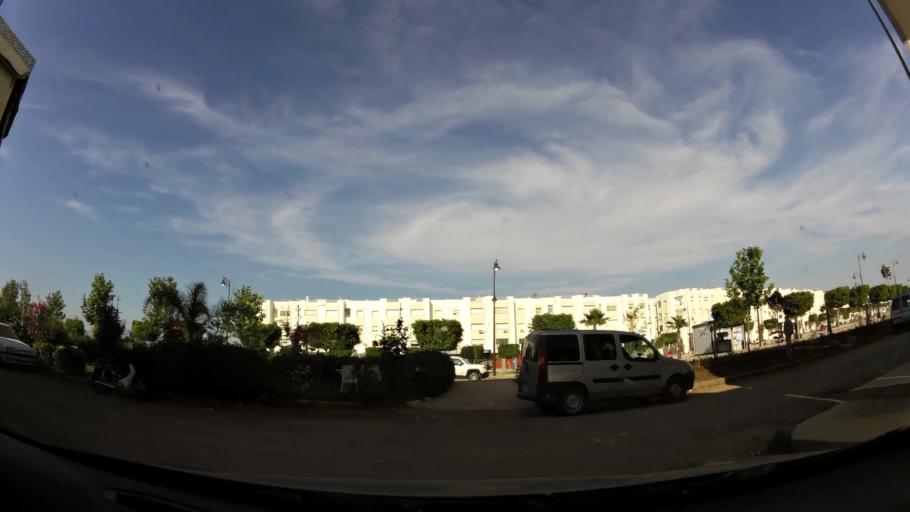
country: MA
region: Fes-Boulemane
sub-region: Fes
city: Fes
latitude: 34.0230
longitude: -5.0275
